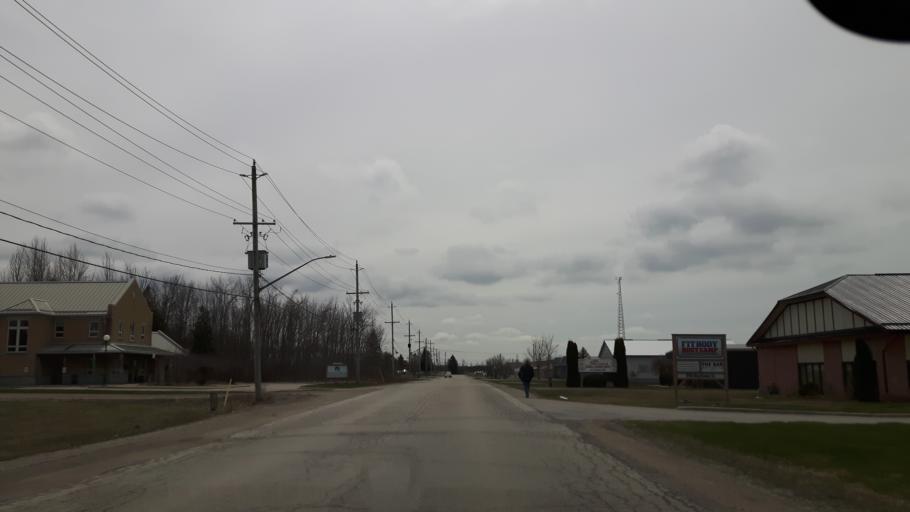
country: CA
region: Ontario
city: Goderich
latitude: 43.7307
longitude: -81.6995
